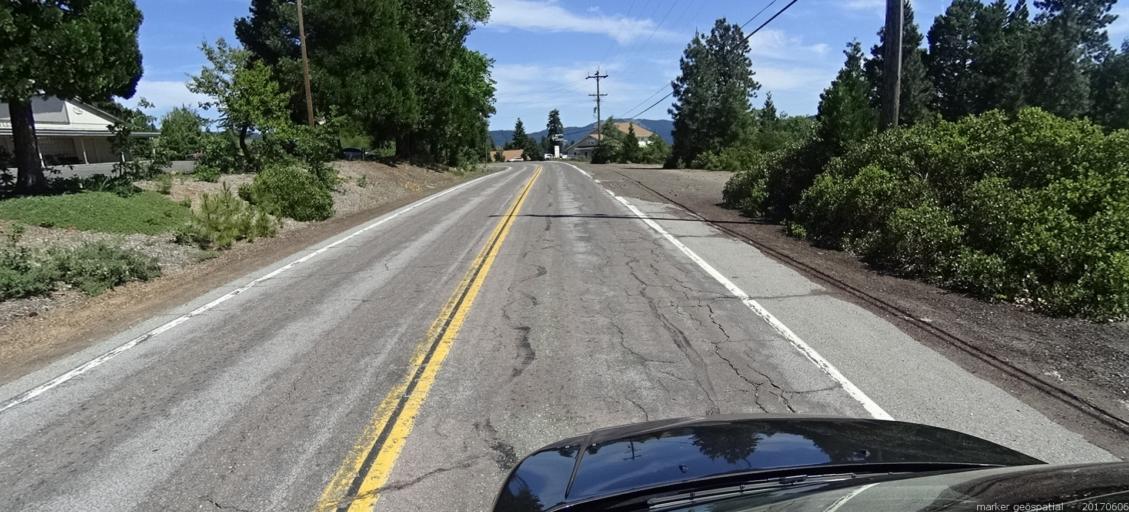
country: US
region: California
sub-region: Siskiyou County
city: Mount Shasta
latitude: 41.2883
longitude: -122.3046
